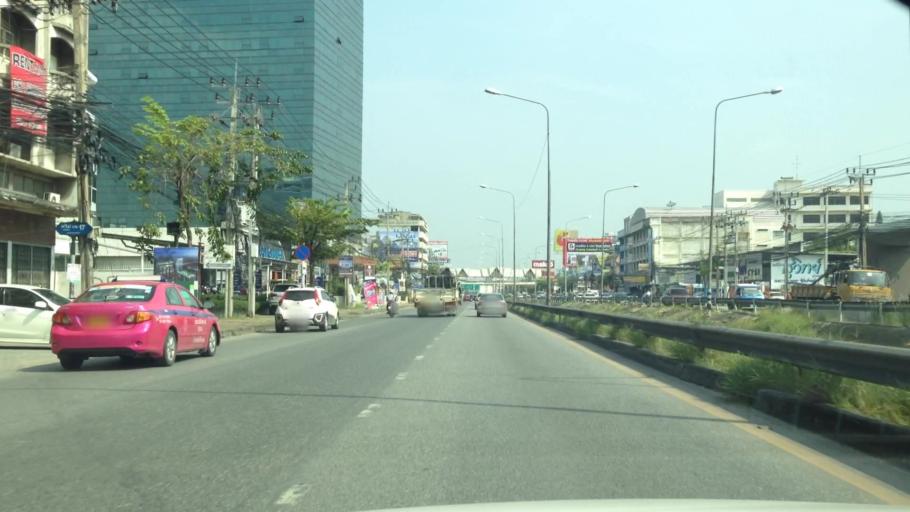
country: TH
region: Bangkok
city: Bang Na
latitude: 13.6467
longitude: 100.6380
